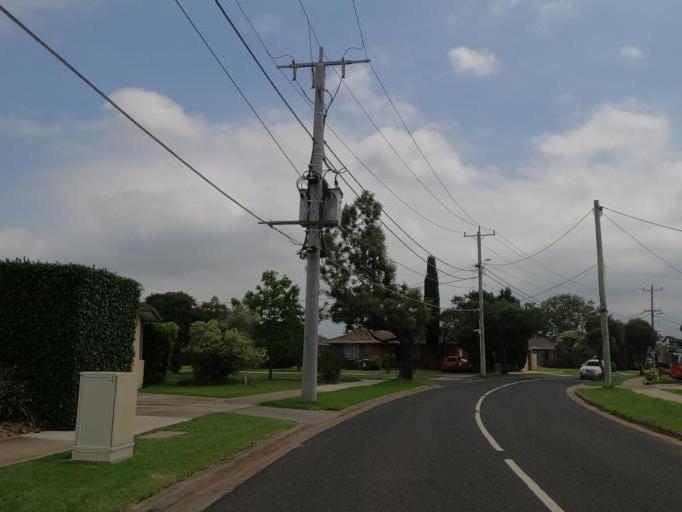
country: AU
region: Victoria
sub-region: Hume
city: Gladstone Park
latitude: -37.6908
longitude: 144.8910
